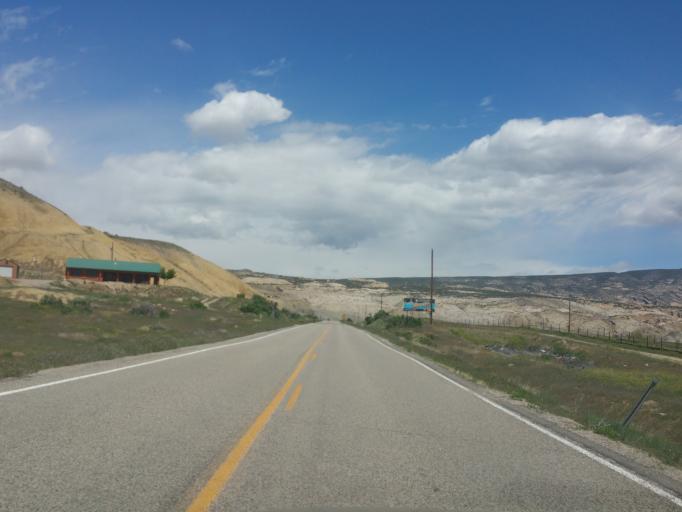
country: US
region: Utah
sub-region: Uintah County
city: Naples
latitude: 40.4224
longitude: -109.3364
